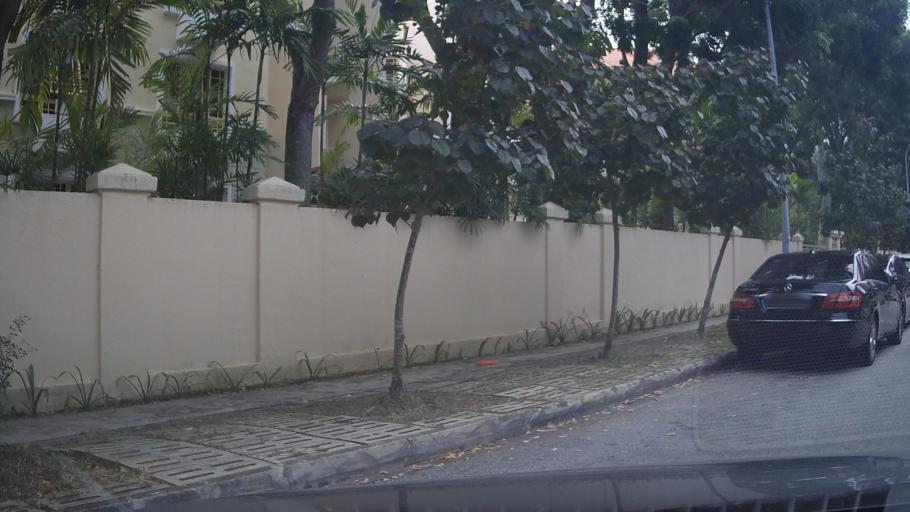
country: SG
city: Singapore
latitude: 1.3105
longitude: 103.9277
